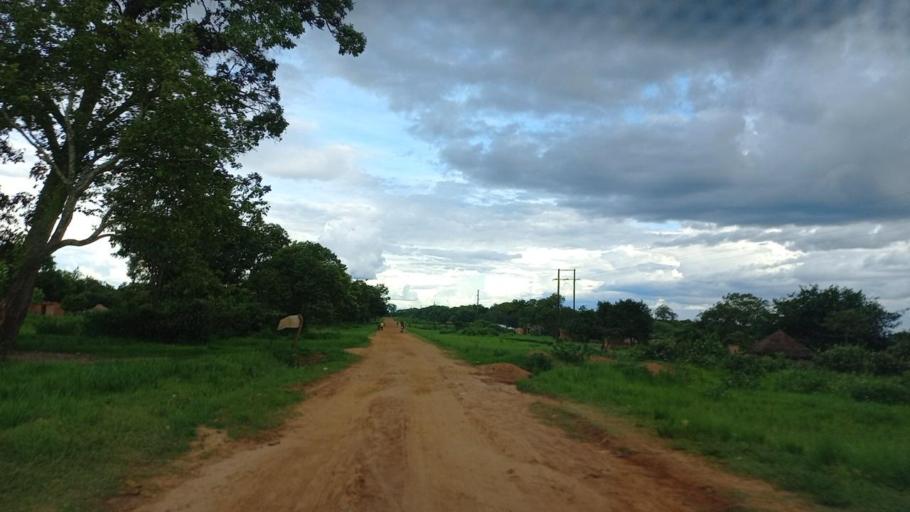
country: ZM
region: North-Western
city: Mwinilunga
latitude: -11.7735
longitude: 24.3964
